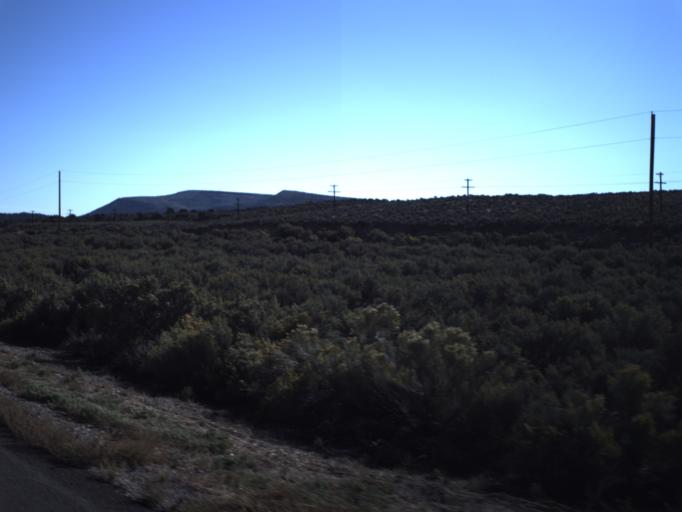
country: US
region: Utah
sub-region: Washington County
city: Enterprise
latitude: 37.7466
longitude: -114.0063
